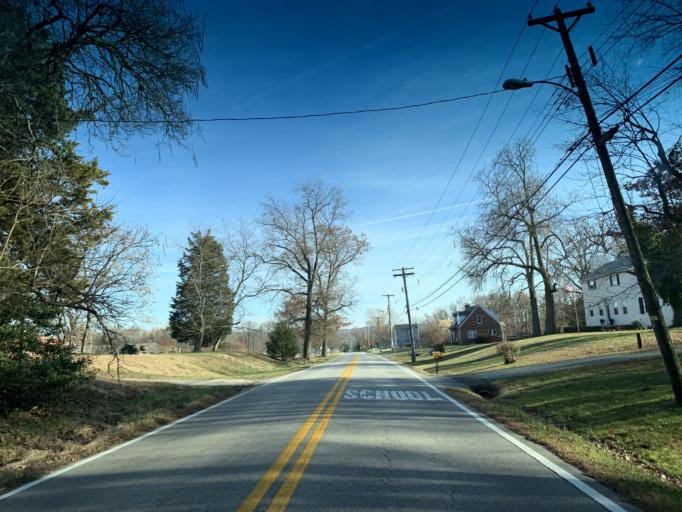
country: US
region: Maryland
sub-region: Cecil County
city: Charlestown
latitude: 39.5743
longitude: -75.9843
